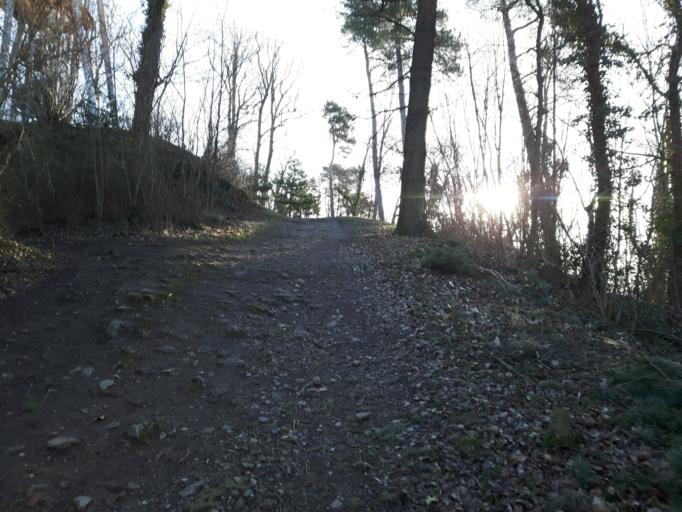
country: DE
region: Baden-Wuerttemberg
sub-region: Freiburg Region
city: Freiburg
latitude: 47.9949
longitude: 7.8615
